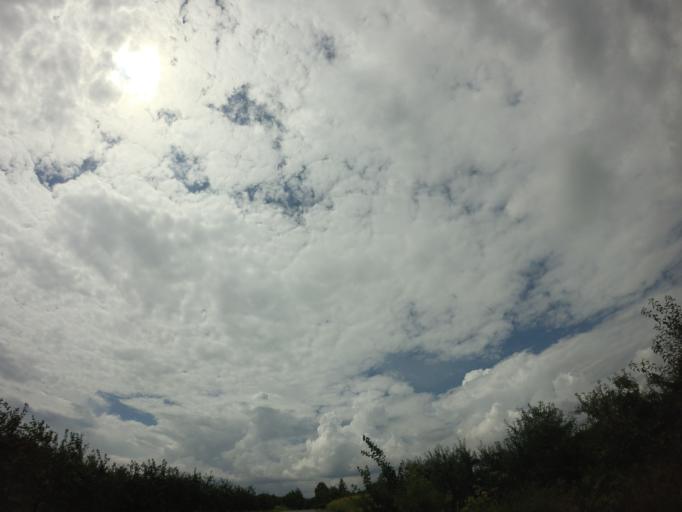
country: PL
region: Lublin Voivodeship
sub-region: Powiat pulawski
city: Kazimierz Dolny
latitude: 51.2743
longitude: 21.9315
